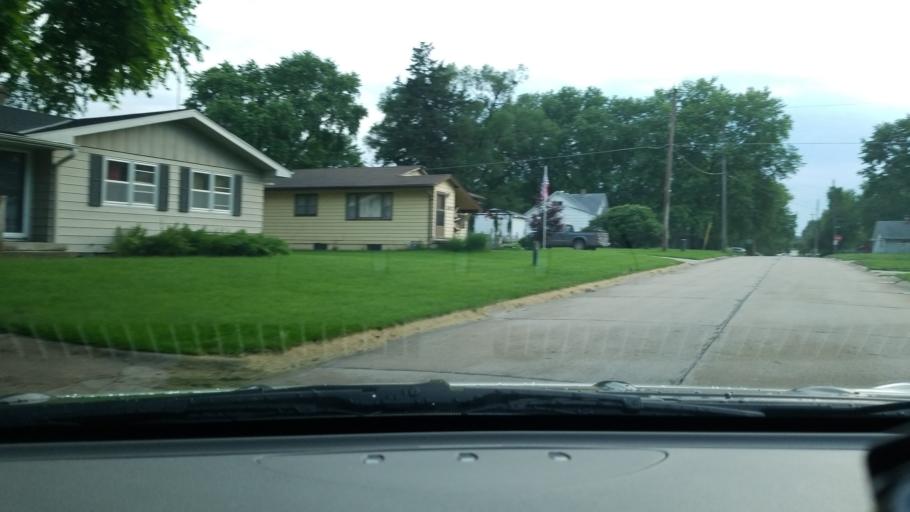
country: US
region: Nebraska
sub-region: Sarpy County
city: Bellevue
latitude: 41.1344
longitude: -95.8896
